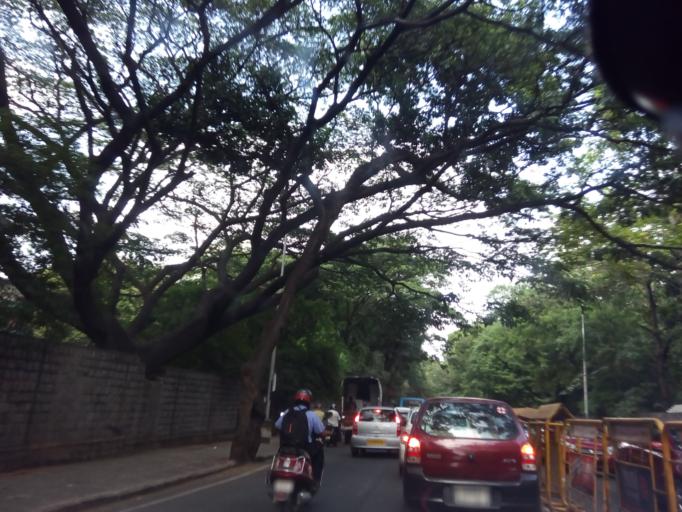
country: IN
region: Karnataka
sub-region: Bangalore Urban
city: Bangalore
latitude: 13.0145
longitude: 77.5710
